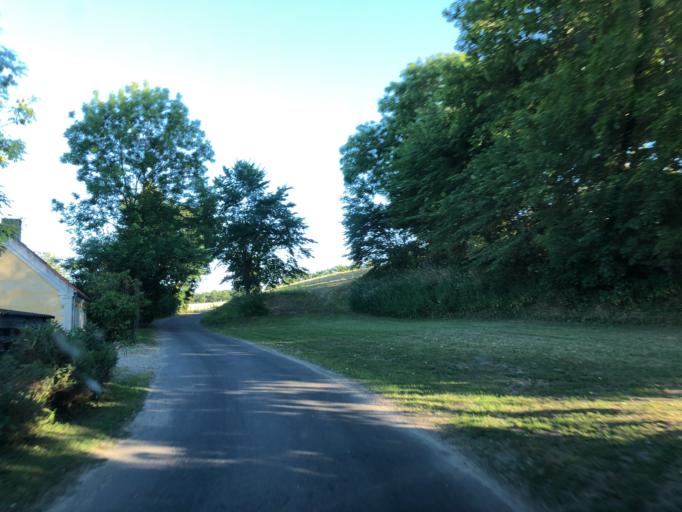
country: DK
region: Central Jutland
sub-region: Horsens Kommune
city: Horsens
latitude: 55.9416
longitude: 9.8658
